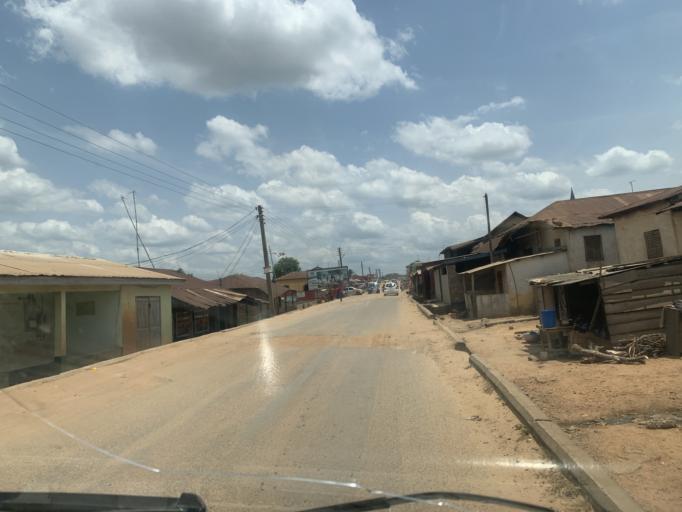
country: GH
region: Central
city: Swedru
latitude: 5.5084
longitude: -0.6930
